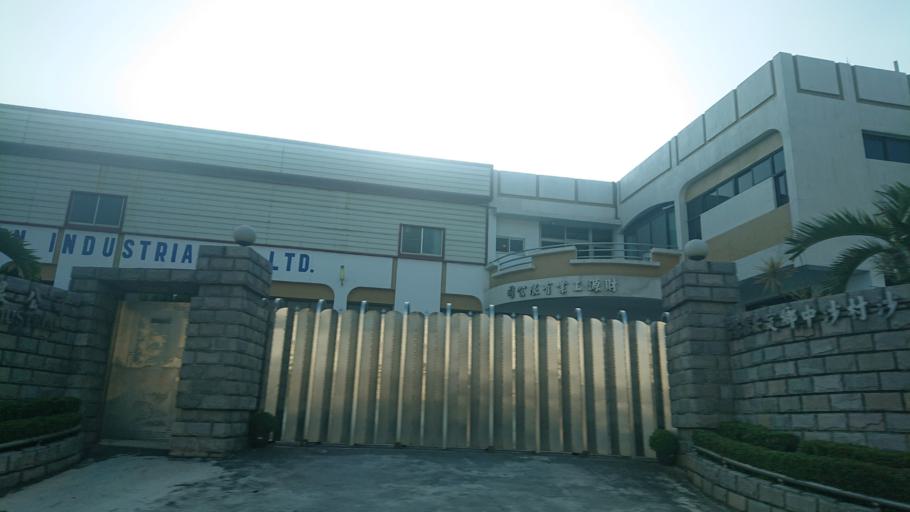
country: TW
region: Taiwan
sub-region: Tainan
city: Tainan
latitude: 23.0746
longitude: 120.2134
